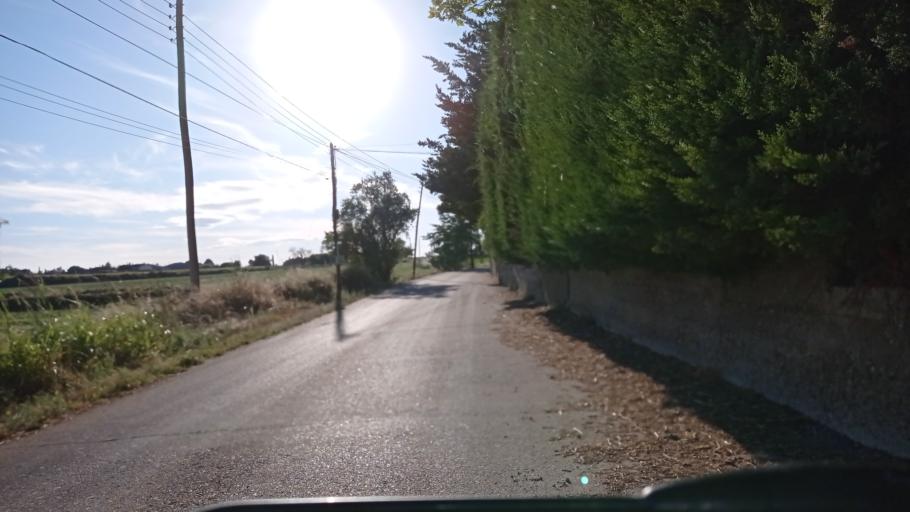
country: ES
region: Aragon
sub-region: Provincia de Zaragoza
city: Oliver-Valdefierro, Oliver, Valdefierro
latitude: 41.6661
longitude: -0.9616
